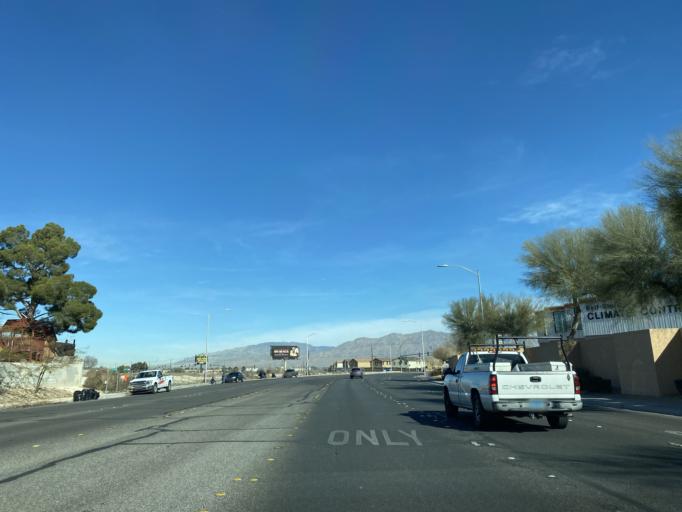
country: US
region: Nevada
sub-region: Clark County
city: Las Vegas
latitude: 36.2294
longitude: -115.2255
